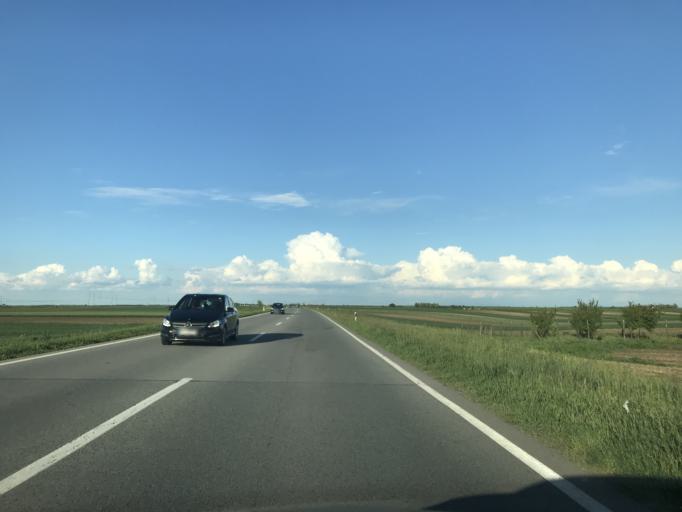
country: RS
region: Autonomna Pokrajina Vojvodina
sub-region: Juznobacki Okrug
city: Petrovaradin
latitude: 45.3212
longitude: 19.9418
